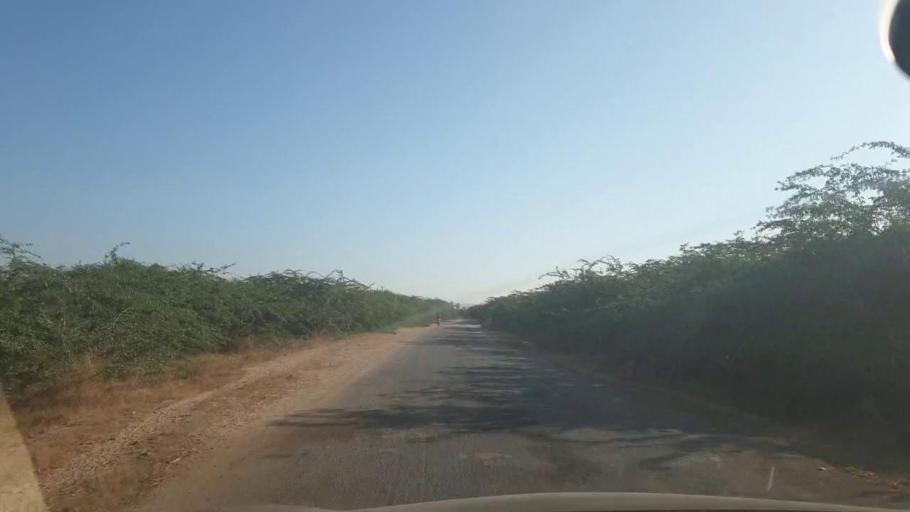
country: PK
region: Sindh
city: Malir Cantonment
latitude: 25.1139
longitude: 67.2710
